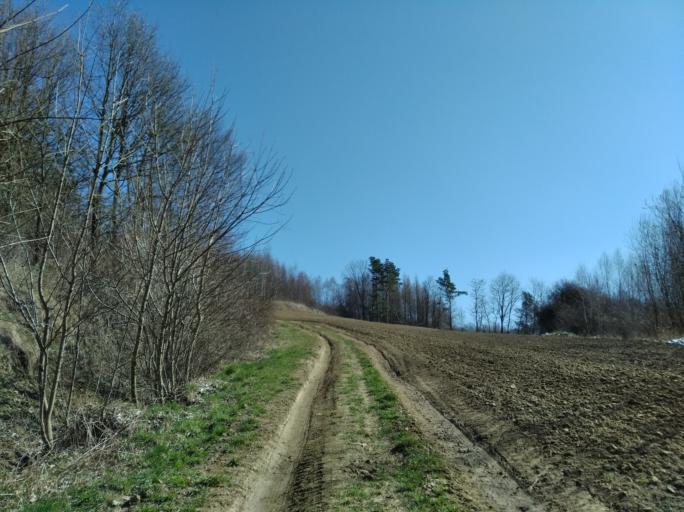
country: PL
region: Subcarpathian Voivodeship
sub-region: Powiat strzyzowski
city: Strzyzow
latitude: 49.8519
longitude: 21.8201
